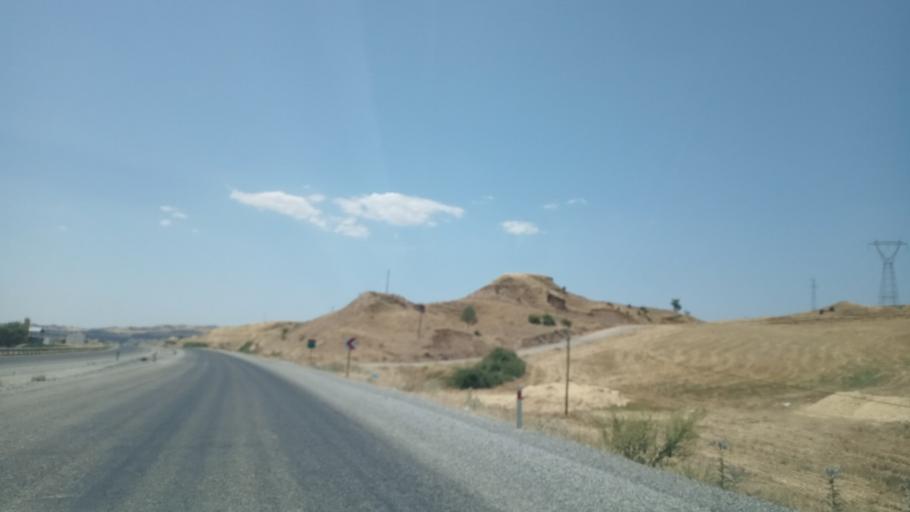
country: TR
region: Batman
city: Kozluk
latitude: 38.1642
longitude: 41.4228
